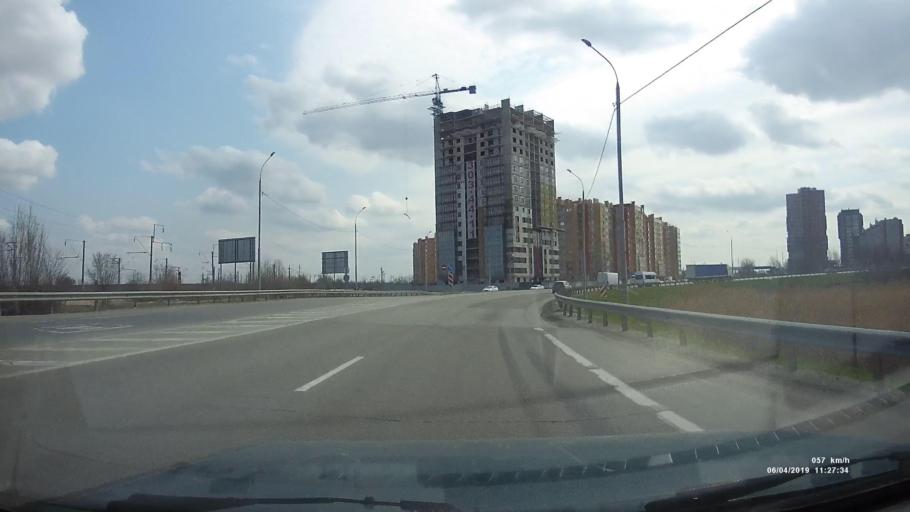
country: RU
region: Rostov
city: Bataysk
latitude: 47.1593
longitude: 39.7435
